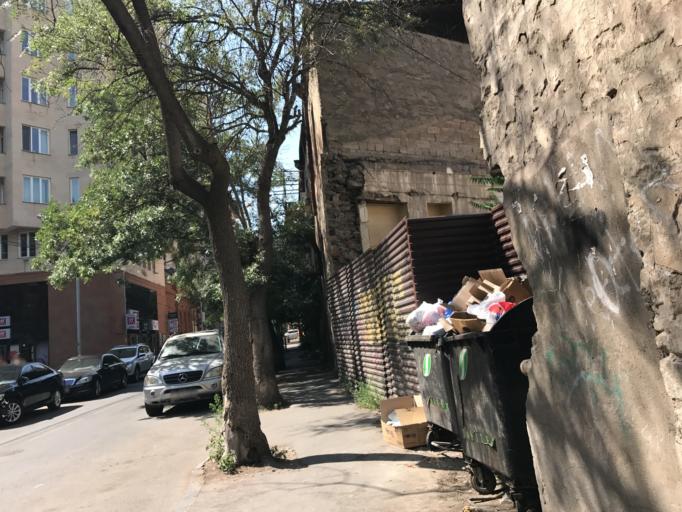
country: AM
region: Yerevan
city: Yerevan
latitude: 40.1801
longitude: 44.5160
